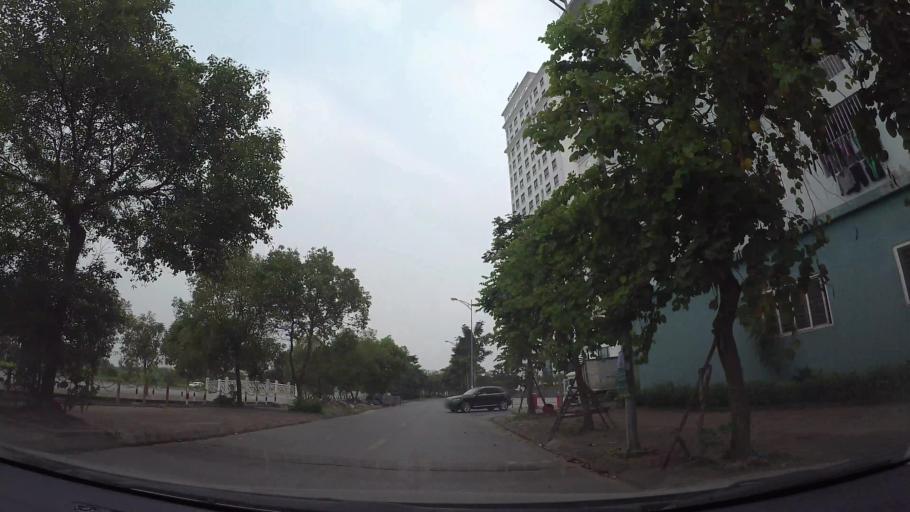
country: VN
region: Ha Noi
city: Trau Quy
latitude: 21.0576
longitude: 105.9137
